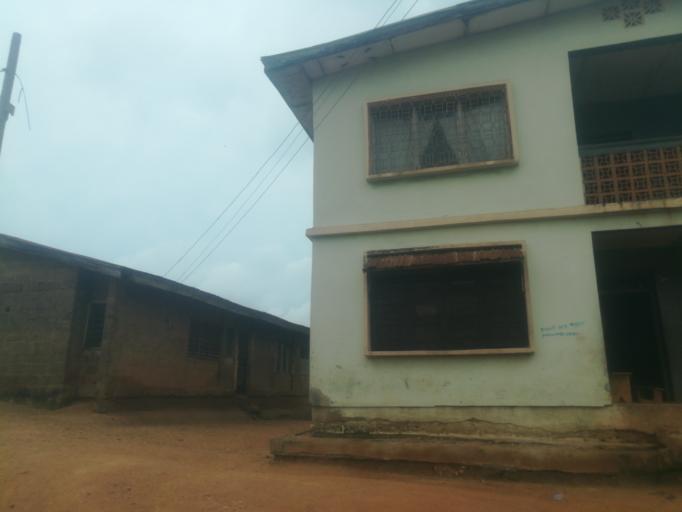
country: NG
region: Oyo
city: Ibadan
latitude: 7.3673
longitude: 3.9266
